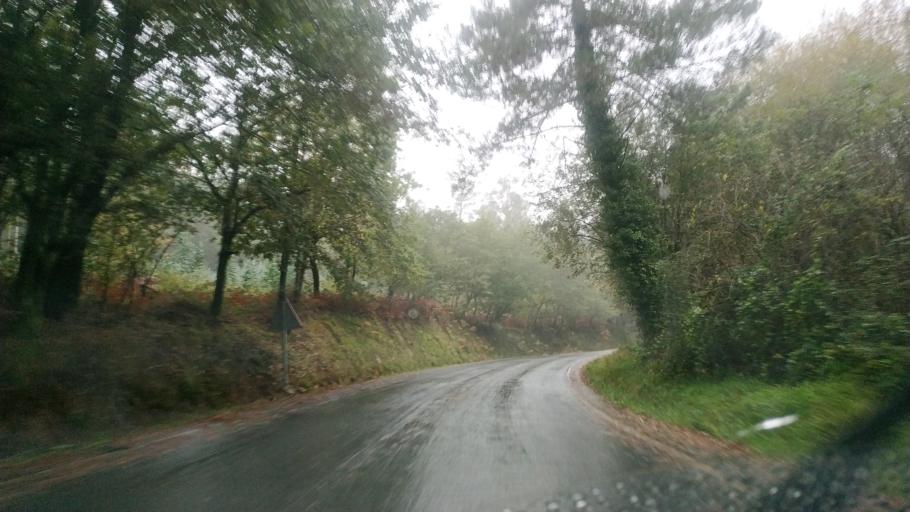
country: ES
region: Galicia
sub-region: Provincia da Coruna
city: Negreira
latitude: 42.9090
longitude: -8.7487
